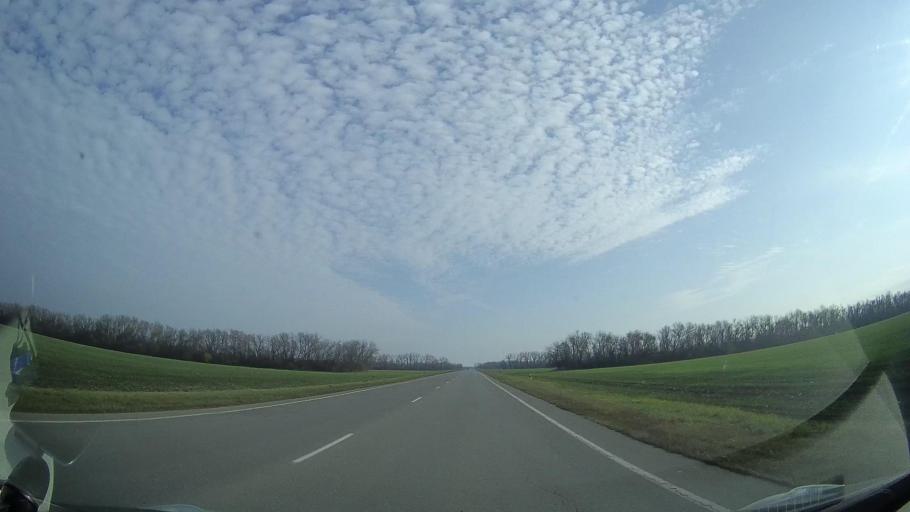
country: RU
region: Rostov
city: Tselina
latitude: 46.5240
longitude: 41.1149
